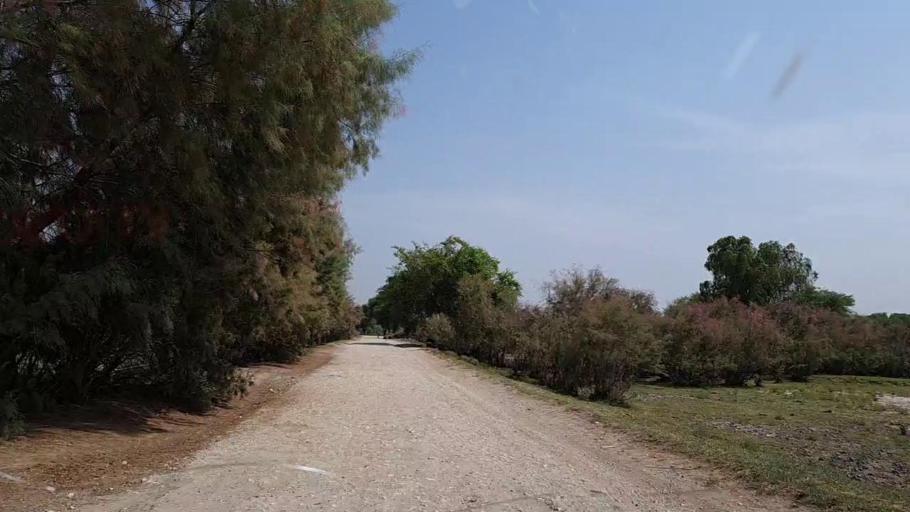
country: PK
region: Sindh
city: Khanpur
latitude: 27.8185
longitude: 69.3052
